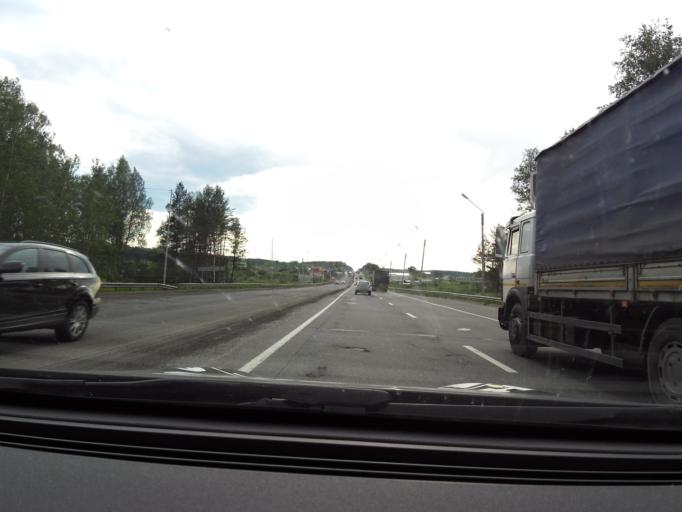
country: RU
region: Vladimir
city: Luknovo
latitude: 56.2369
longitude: 41.9591
